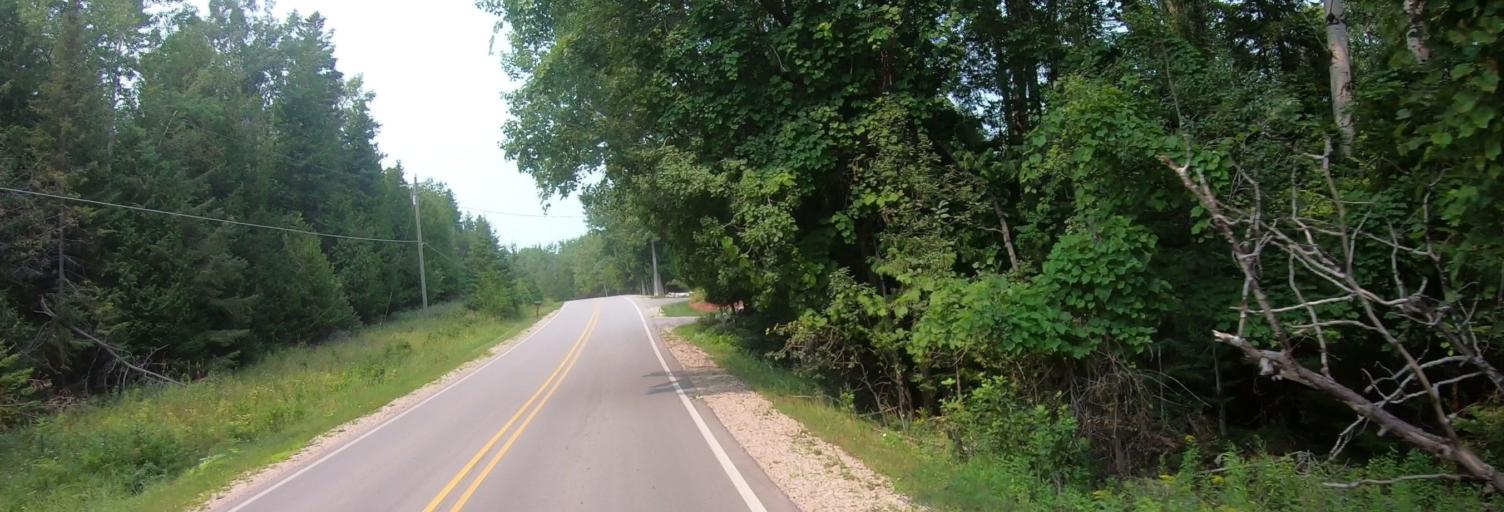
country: CA
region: Ontario
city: Thessalon
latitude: 46.0377
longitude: -83.7099
